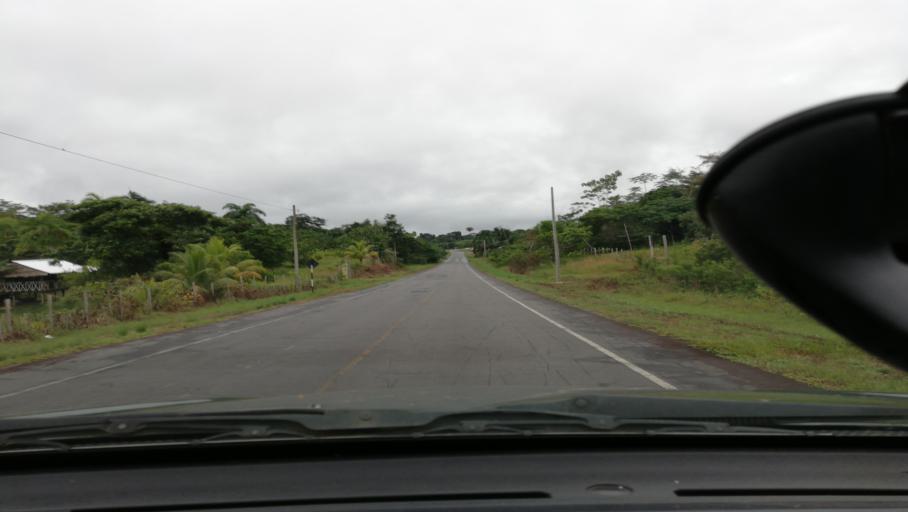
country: PE
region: Loreto
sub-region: Provincia de Loreto
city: Nauta
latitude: -4.3554
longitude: -73.5511
